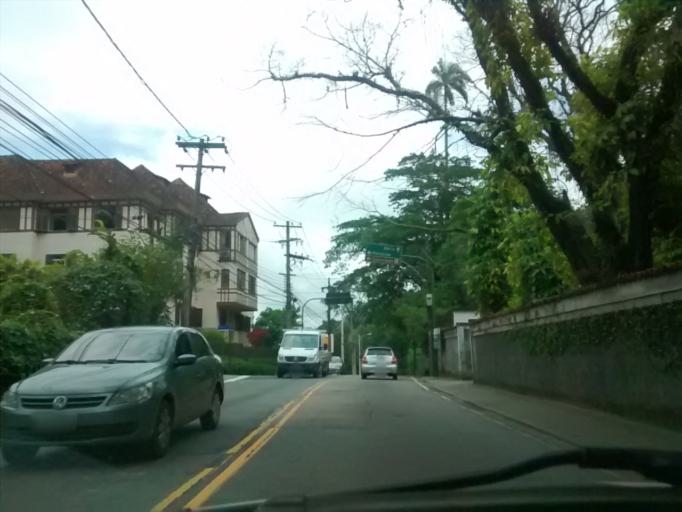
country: BR
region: Rio de Janeiro
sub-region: Rio De Janeiro
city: Rio de Janeiro
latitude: -22.9618
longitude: -43.2736
